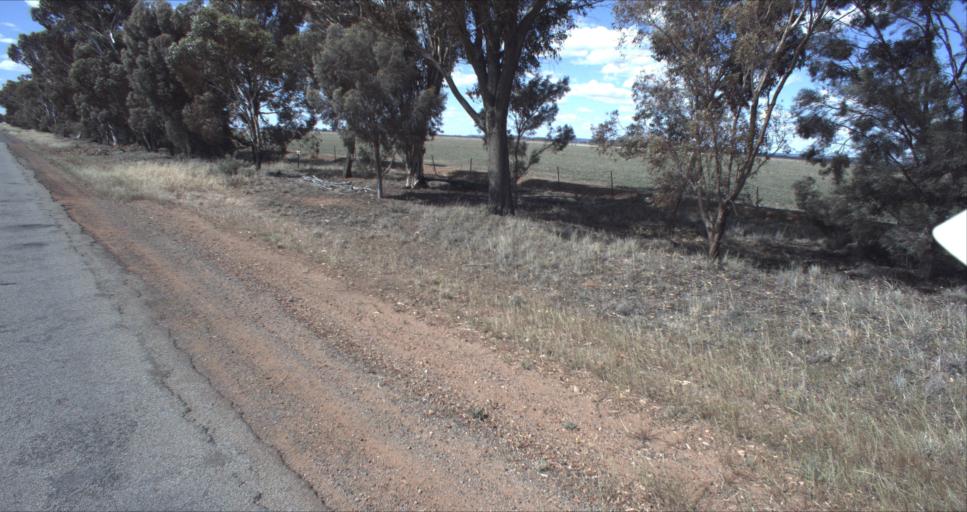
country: AU
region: New South Wales
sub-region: Leeton
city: Leeton
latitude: -34.4745
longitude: 146.2503
